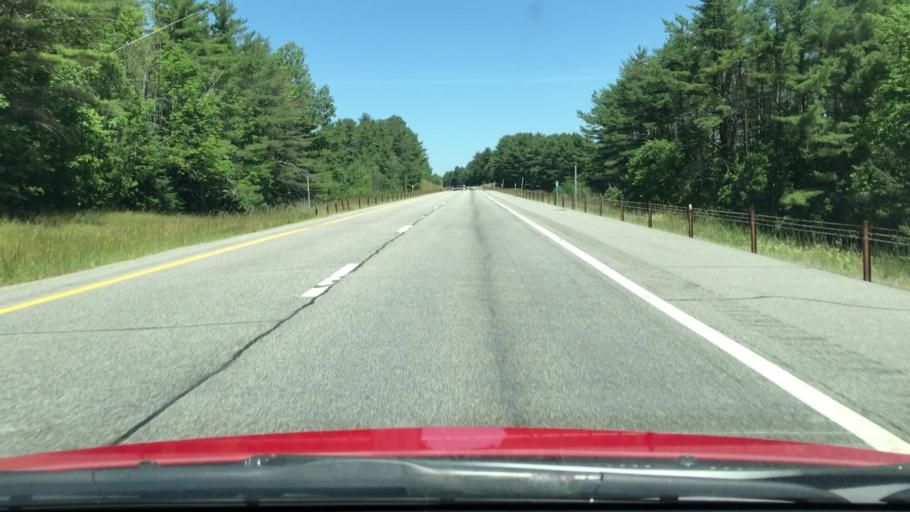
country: US
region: New York
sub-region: Essex County
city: Elizabethtown
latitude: 44.1467
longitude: -73.5833
